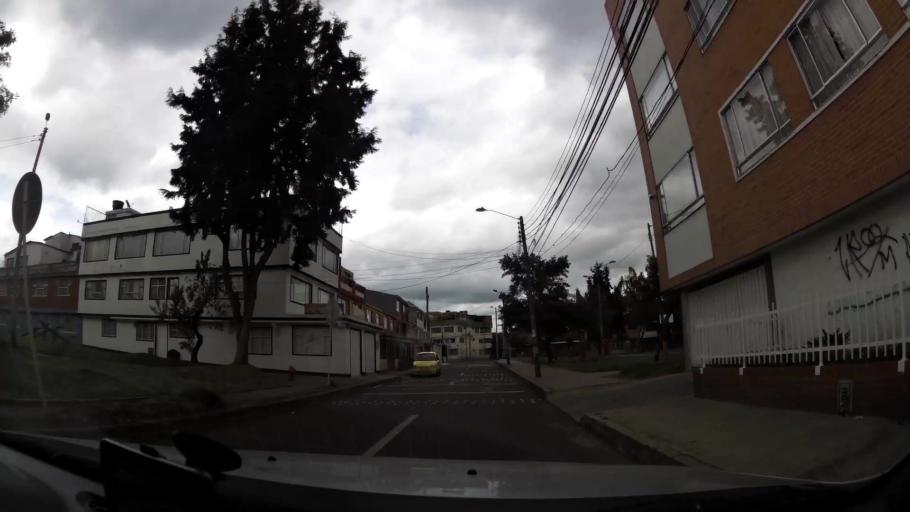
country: CO
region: Bogota D.C.
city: Bogota
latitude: 4.6154
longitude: -74.1221
